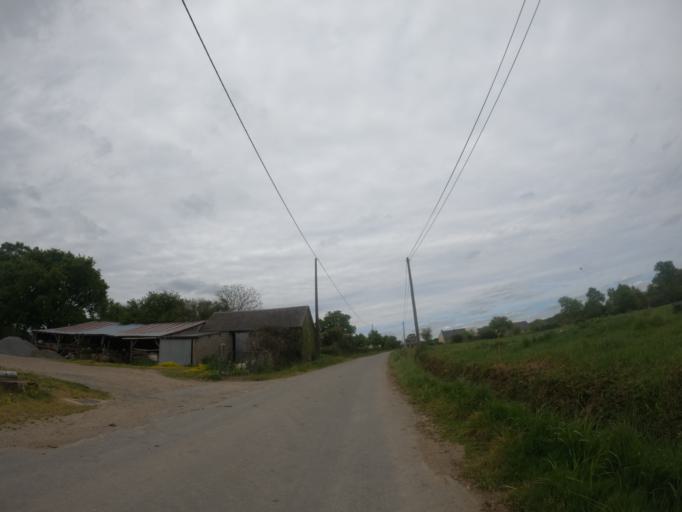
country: FR
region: Pays de la Loire
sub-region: Departement de la Loire-Atlantique
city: Saint-Aubin-des-Chateaux
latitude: 47.7348
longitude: -1.4441
